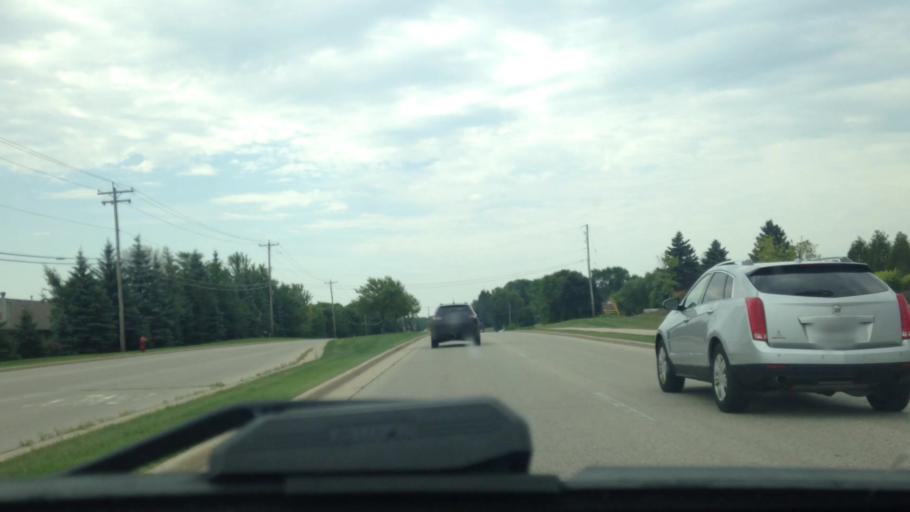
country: US
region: Wisconsin
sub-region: Waukesha County
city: Menomonee Falls
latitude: 43.1378
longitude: -88.1047
